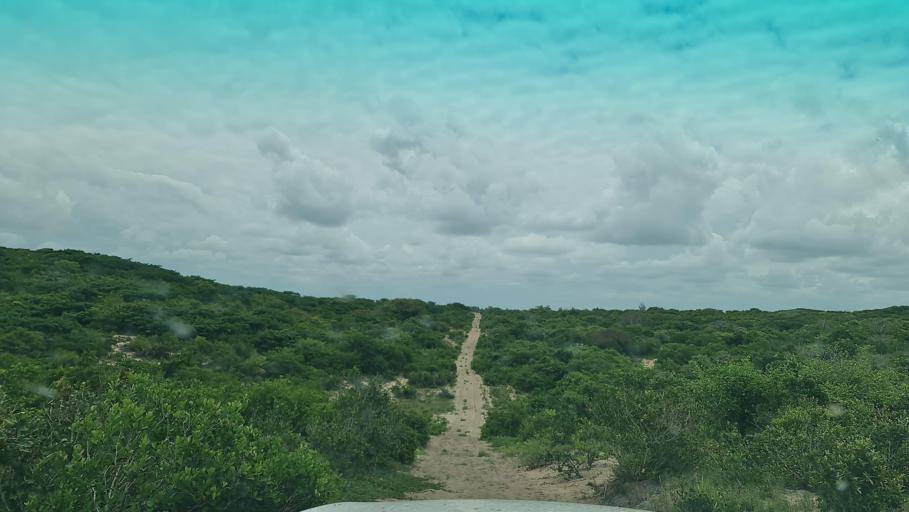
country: MZ
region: Maputo
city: Manhica
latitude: -25.6252
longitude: 32.7811
